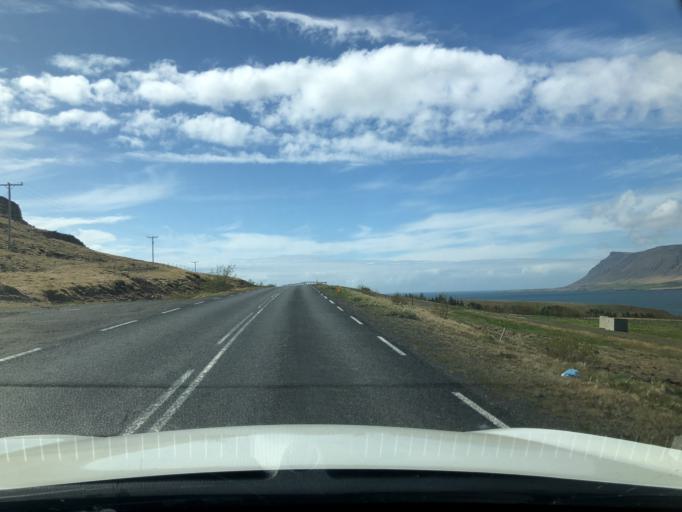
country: IS
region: Capital Region
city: Mosfellsbaer
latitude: 64.3212
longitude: -21.7540
